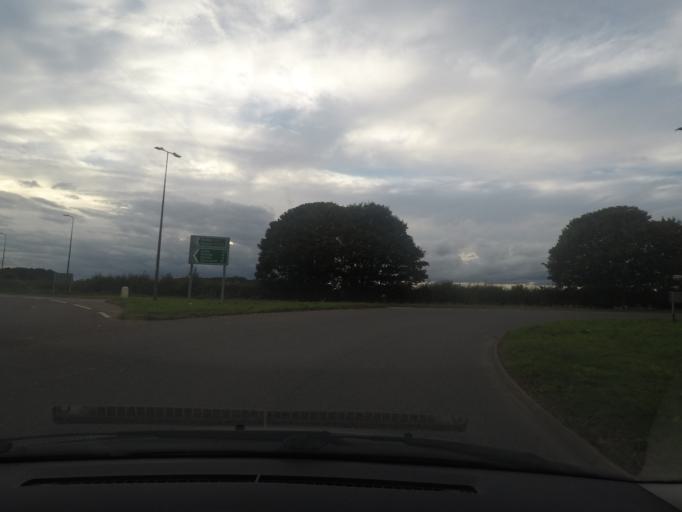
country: GB
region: England
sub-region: Lincolnshire
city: Alford
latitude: 53.2411
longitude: 0.1143
